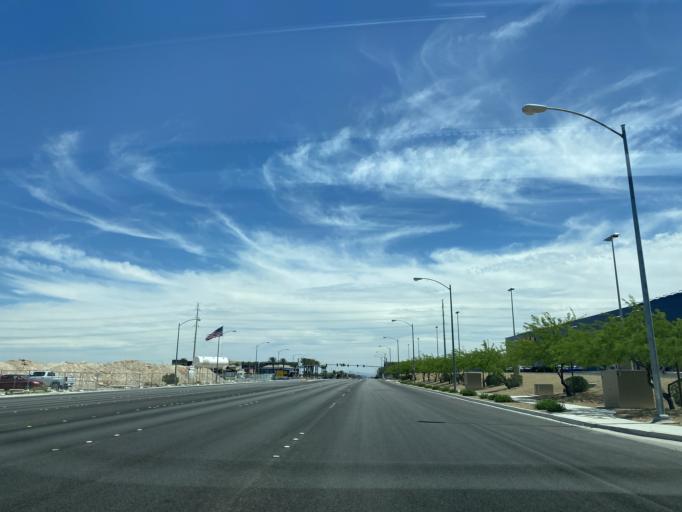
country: US
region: Nevada
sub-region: Clark County
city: Spring Valley
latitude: 36.0703
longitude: -115.2825
